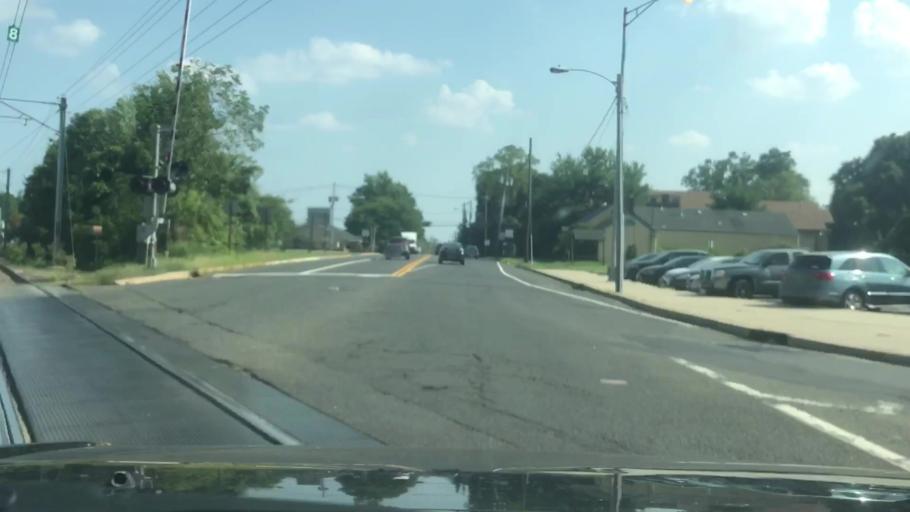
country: US
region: New Jersey
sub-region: Monmouth County
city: Little Silver
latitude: 40.3257
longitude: -74.0392
